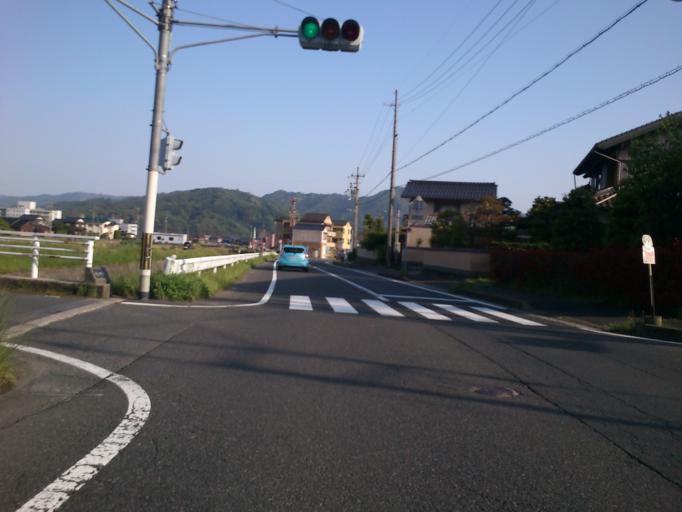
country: JP
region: Kyoto
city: Miyazu
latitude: 35.5742
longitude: 135.1606
